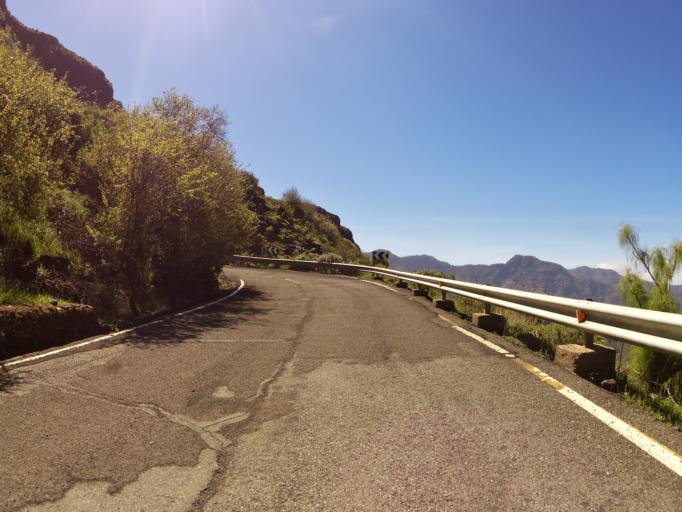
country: ES
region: Canary Islands
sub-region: Provincia de Las Palmas
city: Artenara
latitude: 28.0095
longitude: -15.6886
